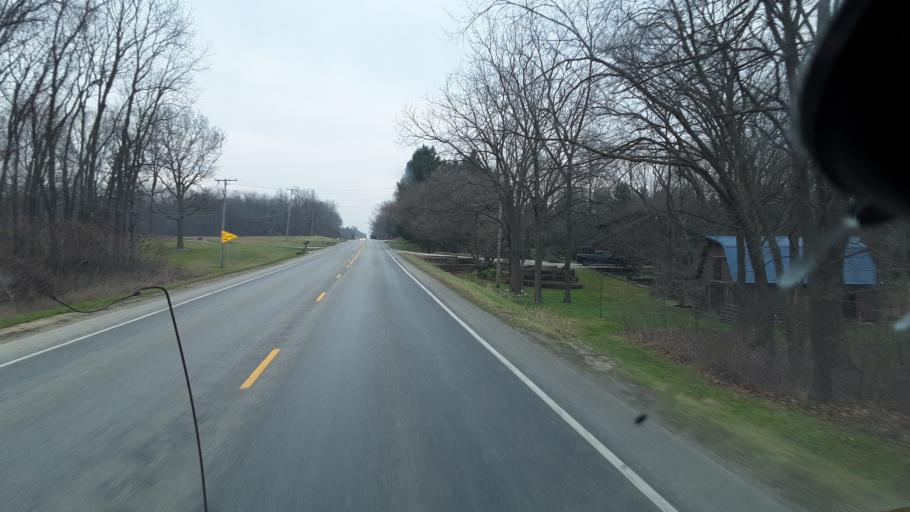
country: US
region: Indiana
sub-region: Elkhart County
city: Middlebury
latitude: 41.7259
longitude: -85.6681
